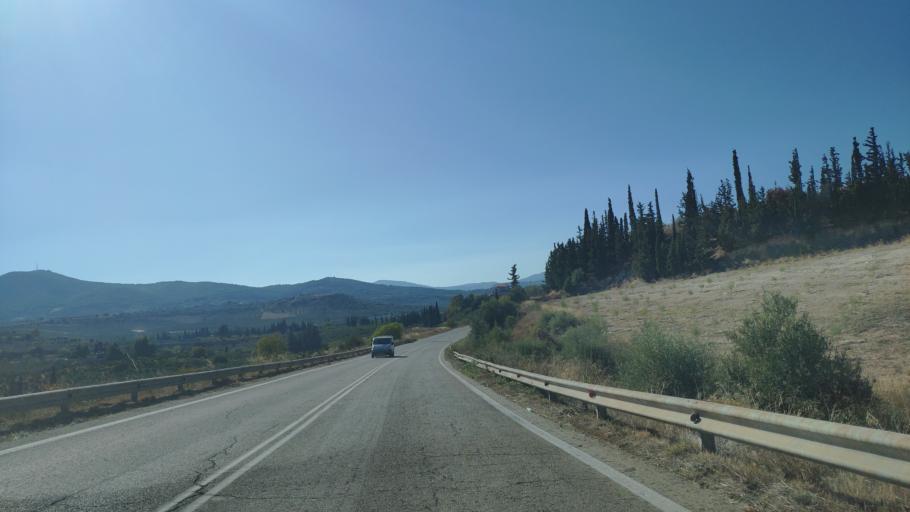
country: GR
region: Peloponnese
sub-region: Nomos Korinthias
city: Arkhaia Korinthos
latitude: 37.9072
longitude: 22.8984
